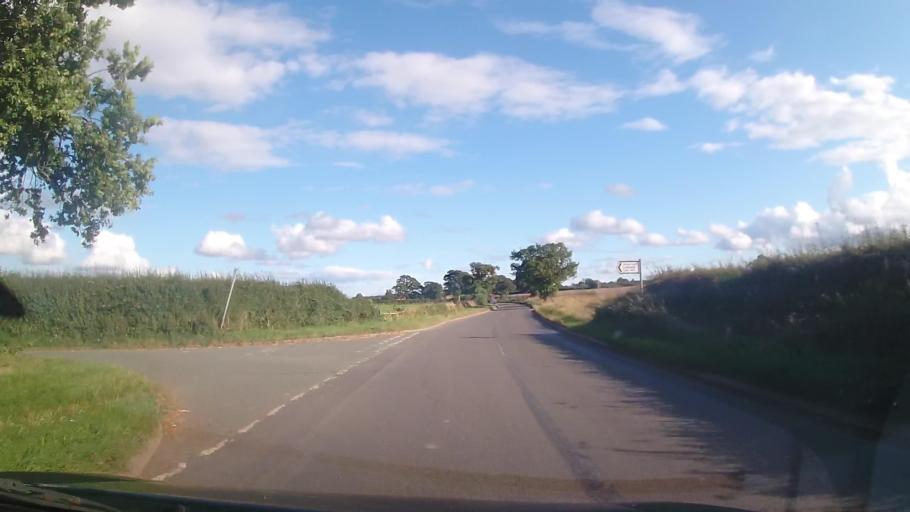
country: GB
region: England
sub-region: Shropshire
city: Great Hanwood
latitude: 52.6578
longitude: -2.8106
